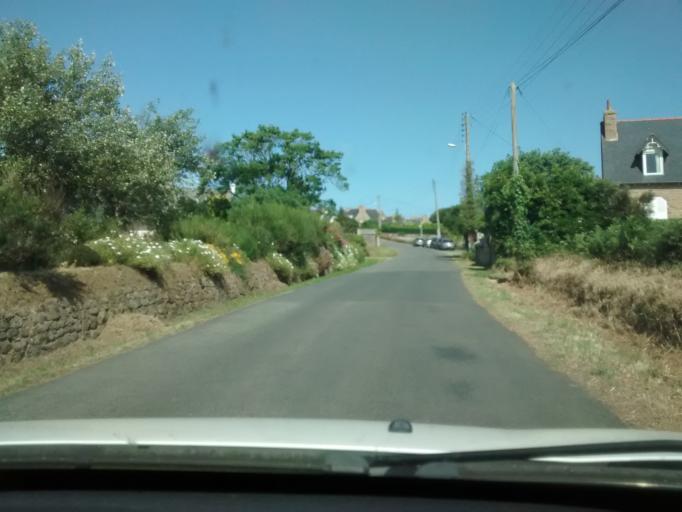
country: FR
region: Brittany
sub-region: Departement des Cotes-d'Armor
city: Trevou-Treguignec
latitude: 48.8308
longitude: -3.3224
